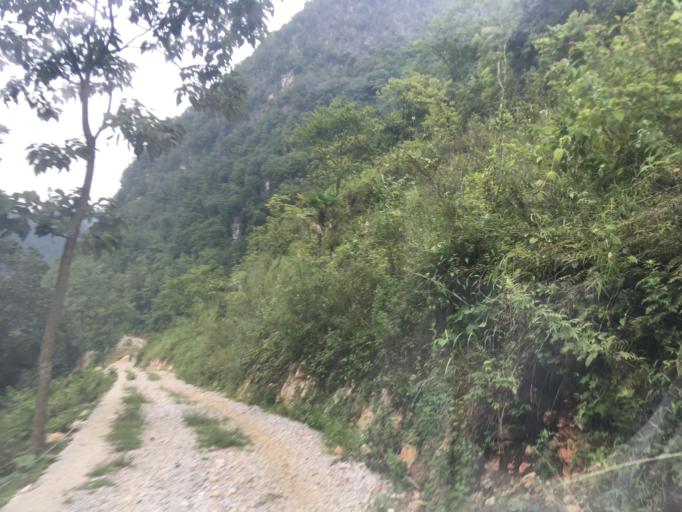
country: CN
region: Guangxi Zhuangzu Zizhiqu
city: Xinzhou
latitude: 25.2193
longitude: 105.6283
